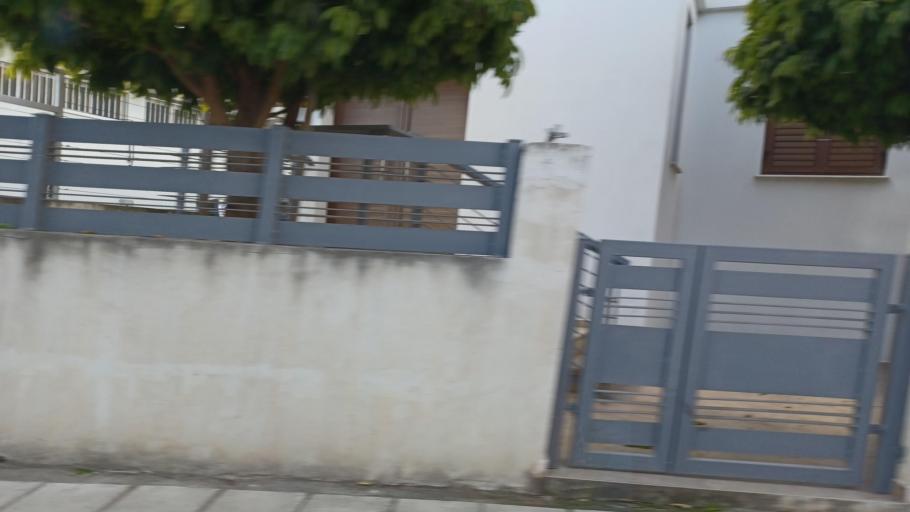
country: CY
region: Limassol
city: Pano Polemidia
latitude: 34.6934
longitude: 33.0021
